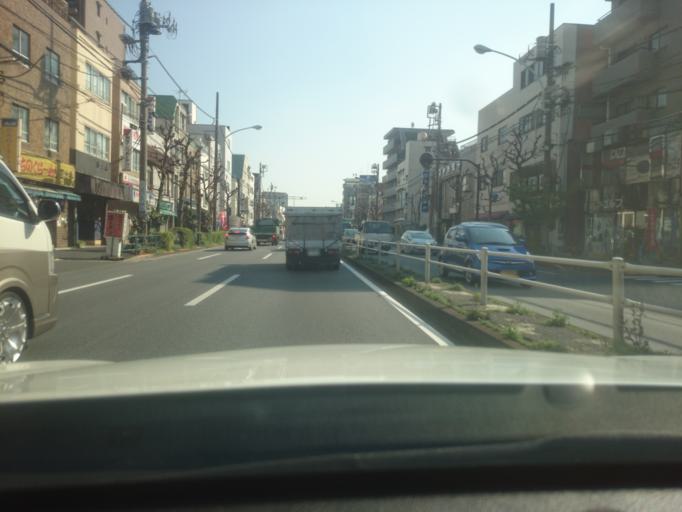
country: JP
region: Tokyo
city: Musashino
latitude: 35.6984
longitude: 139.6175
